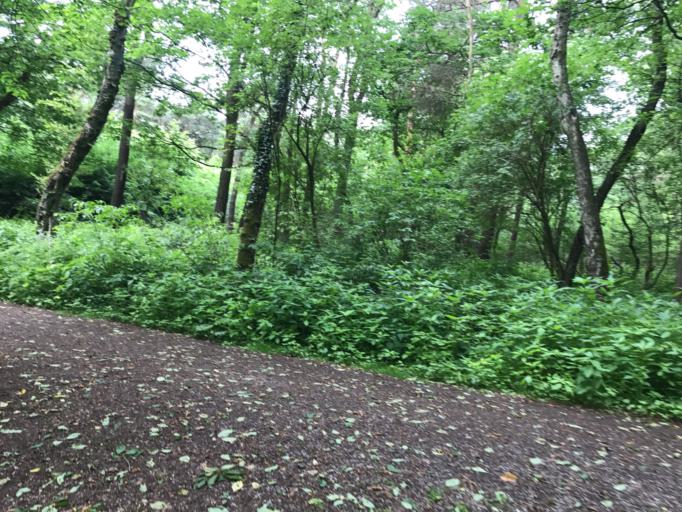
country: DE
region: North Rhine-Westphalia
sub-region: Regierungsbezirk Dusseldorf
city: Duisburg
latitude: 51.4227
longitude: 6.8209
